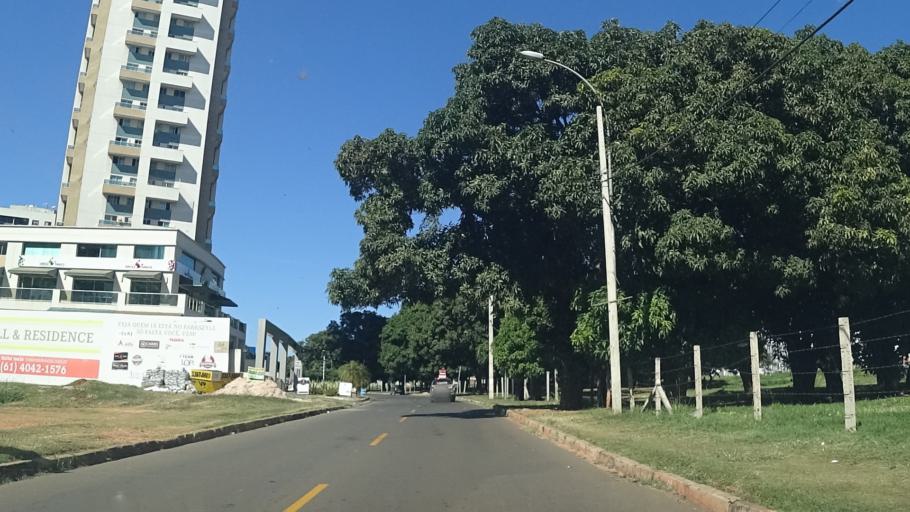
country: BR
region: Federal District
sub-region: Brasilia
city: Brasilia
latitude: -15.8432
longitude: -48.0300
